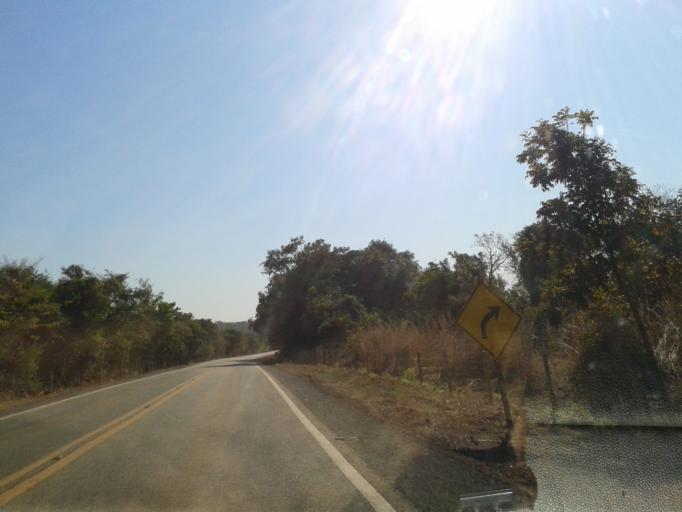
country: BR
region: Goias
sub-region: Mozarlandia
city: Mozarlandia
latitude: -14.6634
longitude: -50.5312
